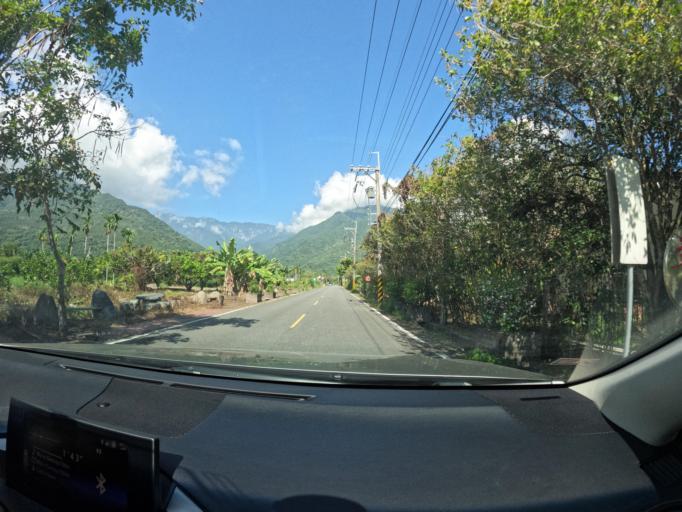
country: TW
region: Taiwan
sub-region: Hualien
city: Hualian
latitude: 23.5802
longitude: 121.3708
